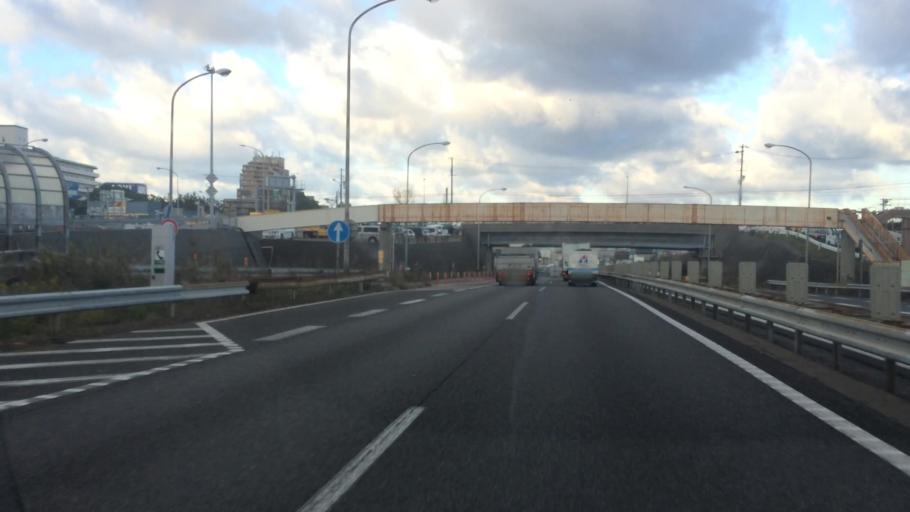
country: JP
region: Hyogo
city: Akashi
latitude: 34.6477
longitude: 135.0533
